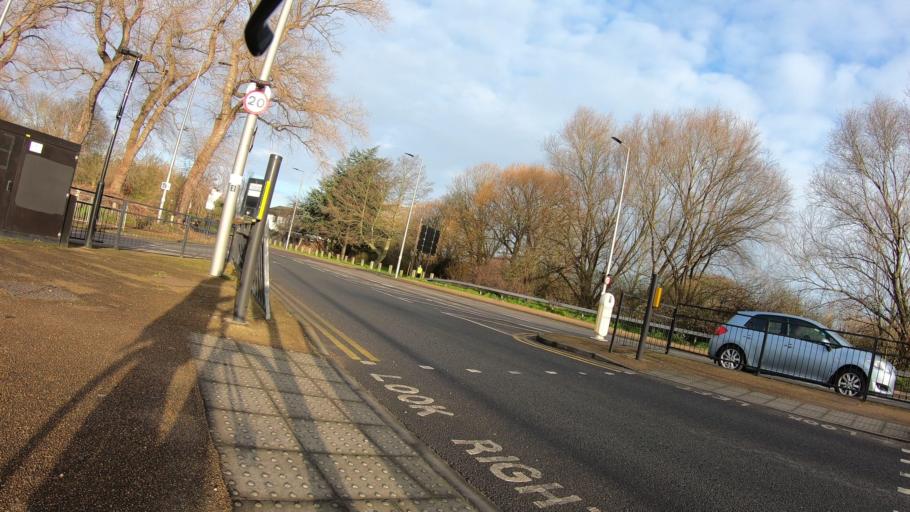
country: GB
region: England
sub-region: Greater London
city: Hackney
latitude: 51.5485
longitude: -0.0196
